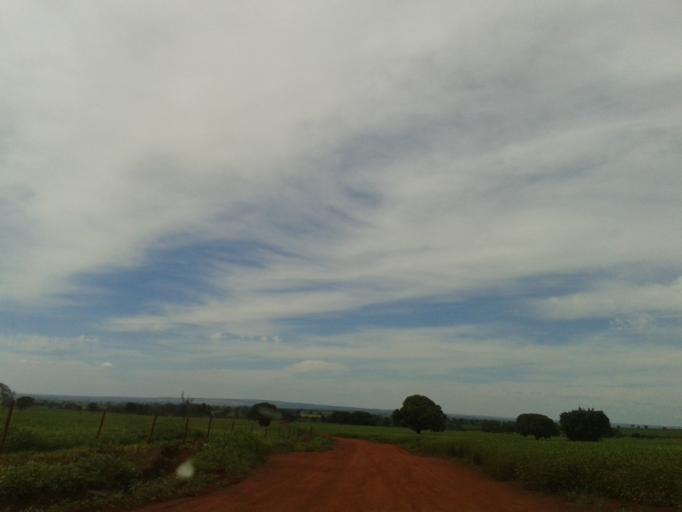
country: BR
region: Minas Gerais
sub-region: Capinopolis
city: Capinopolis
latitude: -18.7426
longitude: -49.8450
